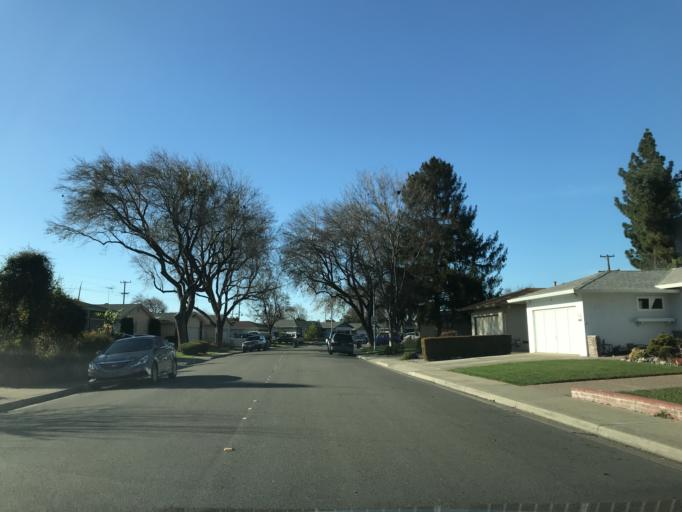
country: US
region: California
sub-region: Santa Clara County
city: Milpitas
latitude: 37.4297
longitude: -121.9152
